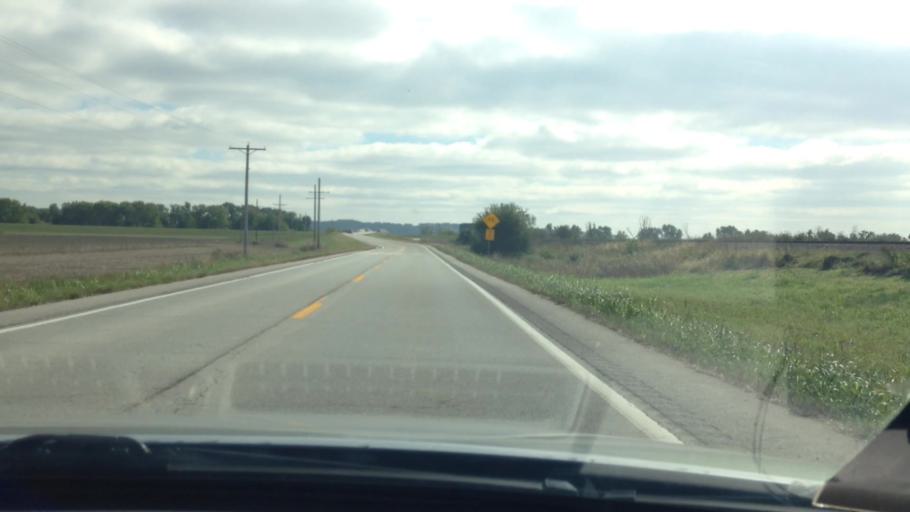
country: US
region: Kansas
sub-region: Leavenworth County
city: Lansing
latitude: 39.2778
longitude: -94.8315
